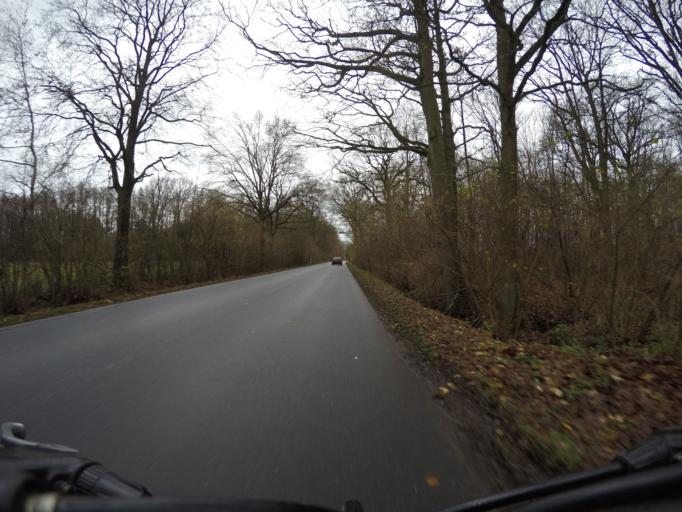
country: DE
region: Schleswig-Holstein
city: Hasloh
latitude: 53.7015
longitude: 9.8762
